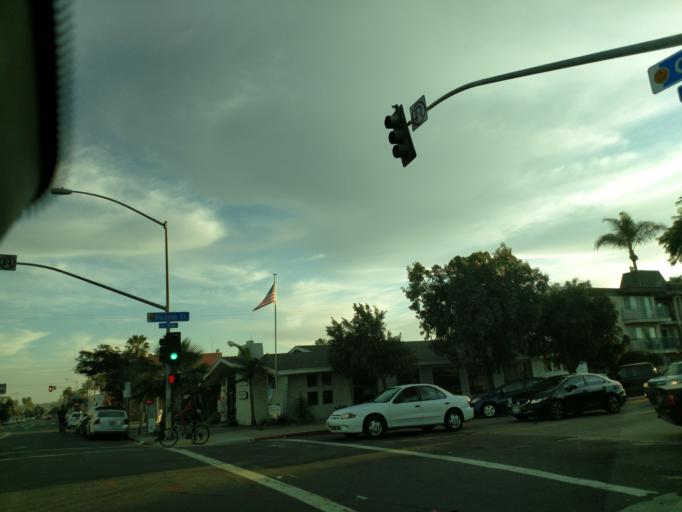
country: US
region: California
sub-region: San Diego County
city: La Jolla
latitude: 32.7984
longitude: -117.2522
